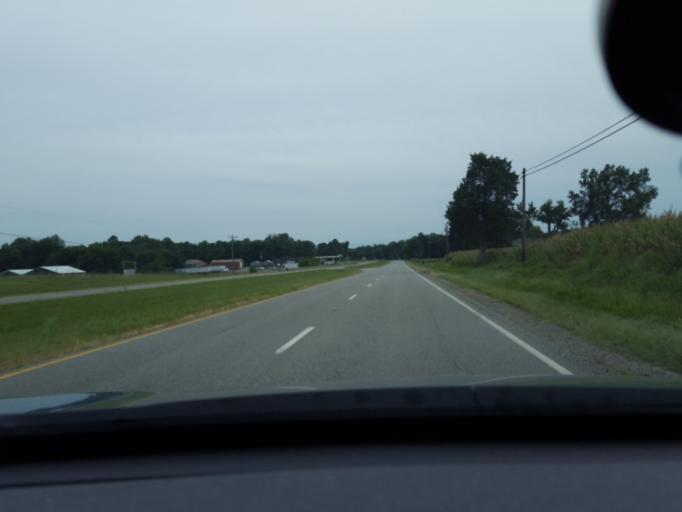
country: US
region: Virginia
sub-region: Caroline County
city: Bowling Green
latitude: 38.0161
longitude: -77.3373
